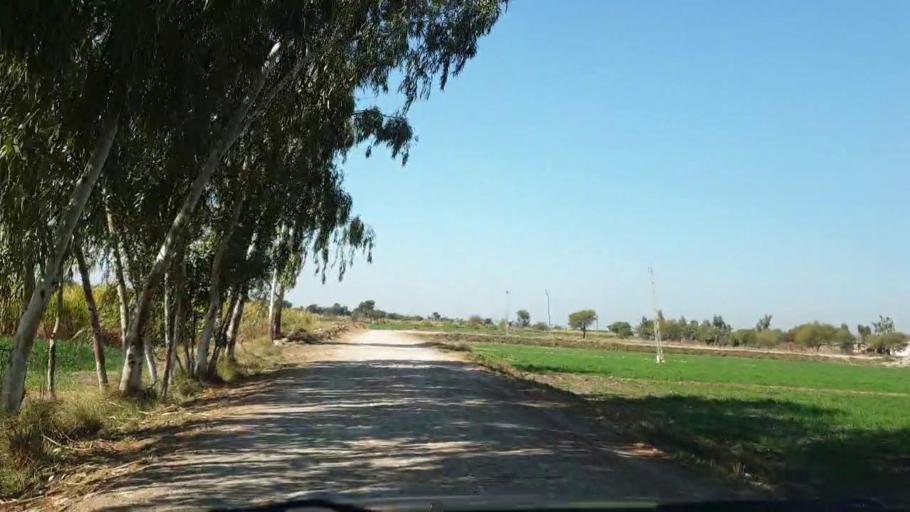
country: PK
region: Sindh
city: Sinjhoro
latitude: 26.1098
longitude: 68.8409
